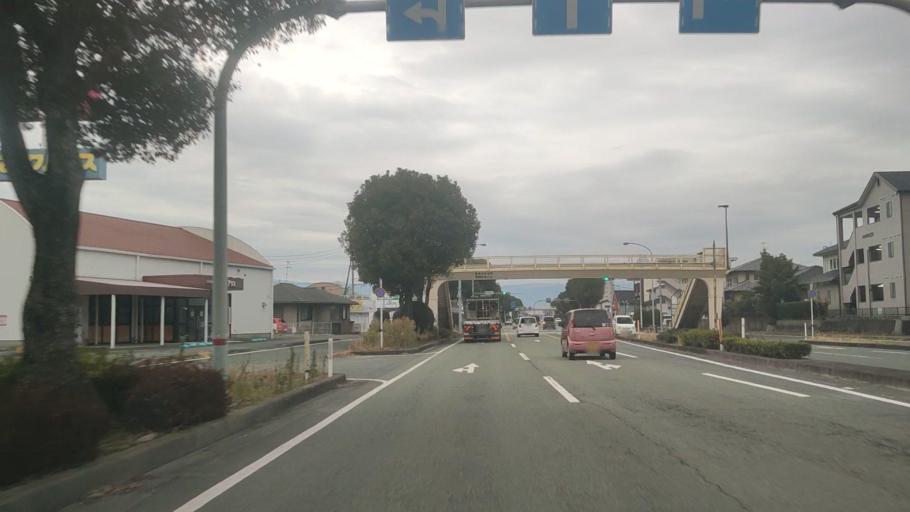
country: JP
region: Kumamoto
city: Ozu
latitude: 32.8581
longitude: 130.7933
